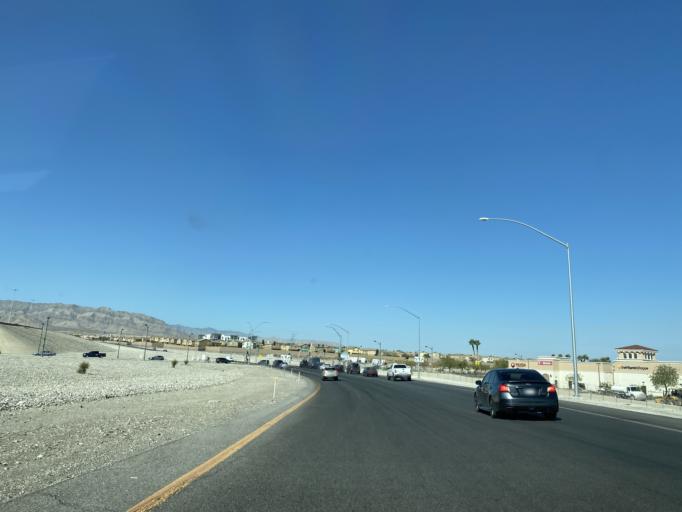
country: US
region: Nevada
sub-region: Clark County
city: Summerlin South
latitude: 36.2800
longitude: -115.2860
